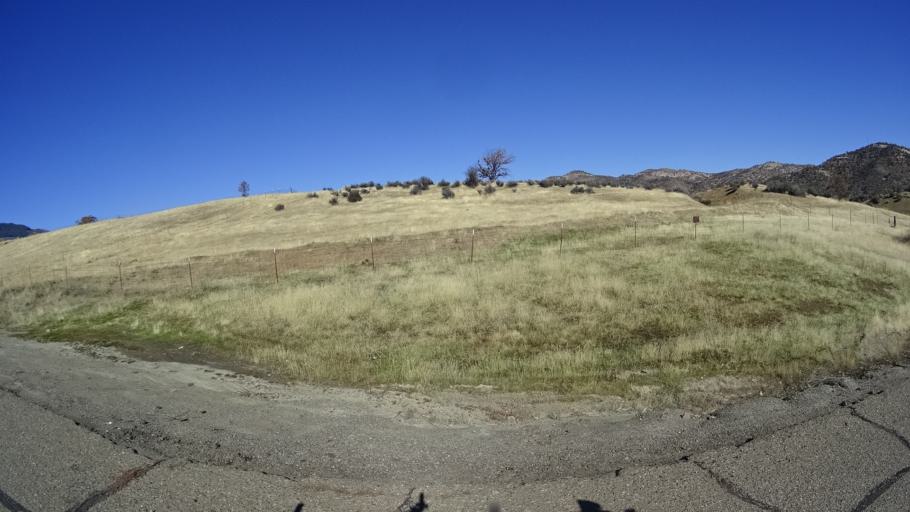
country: US
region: California
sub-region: Siskiyou County
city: Yreka
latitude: 41.9193
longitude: -122.5773
